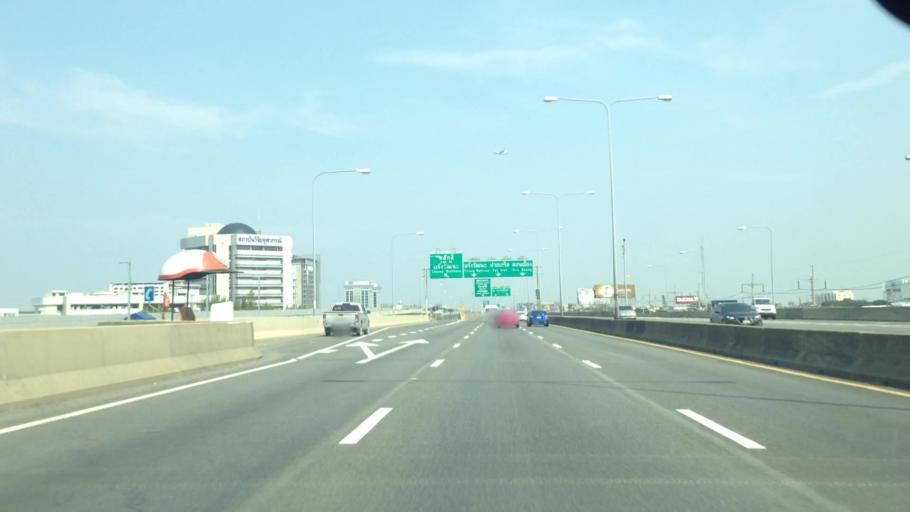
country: TH
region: Bangkok
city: Lak Si
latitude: 13.8761
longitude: 100.5768
